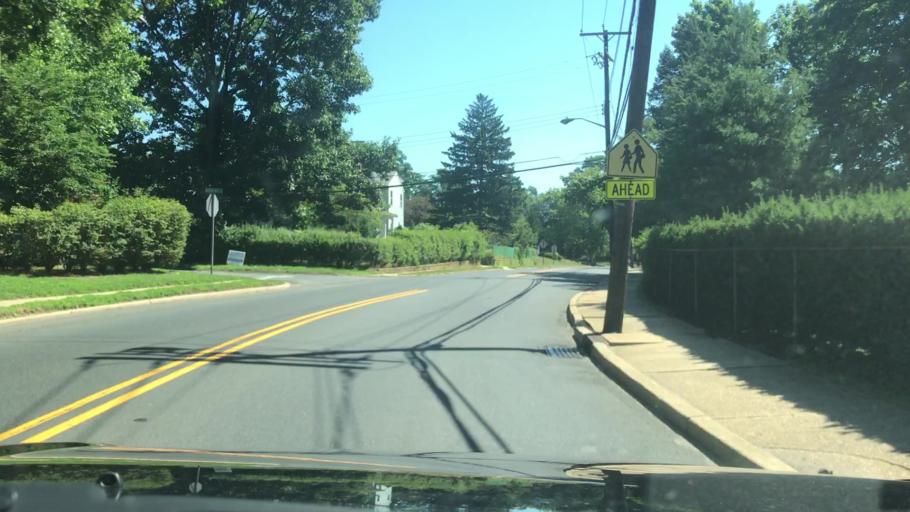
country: US
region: New Jersey
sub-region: Monmouth County
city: Red Bank
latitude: 40.3484
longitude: -74.0861
